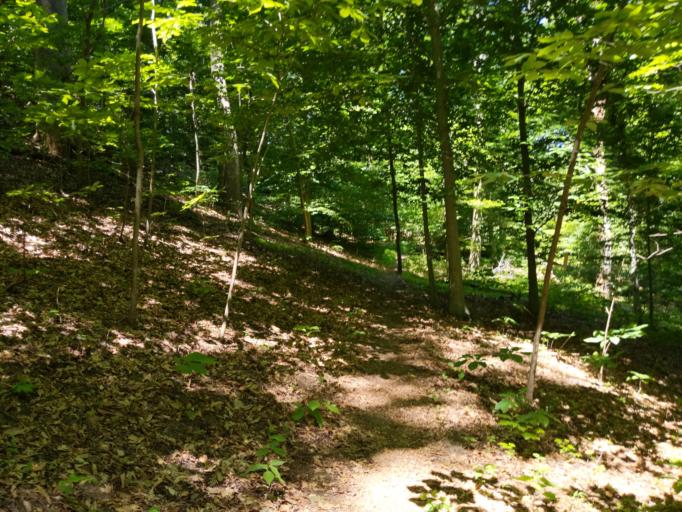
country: US
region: Virginia
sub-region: Westmoreland County
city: Montross
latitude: 38.1694
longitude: -76.8773
